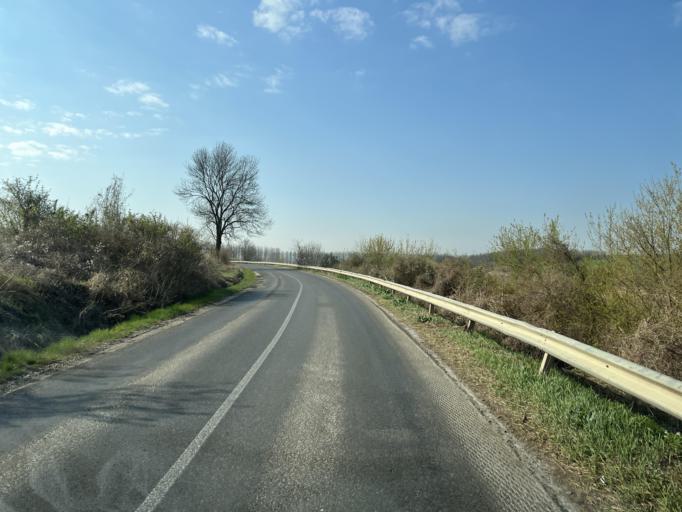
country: HU
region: Pest
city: Galgamacsa
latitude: 47.7328
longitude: 19.3744
